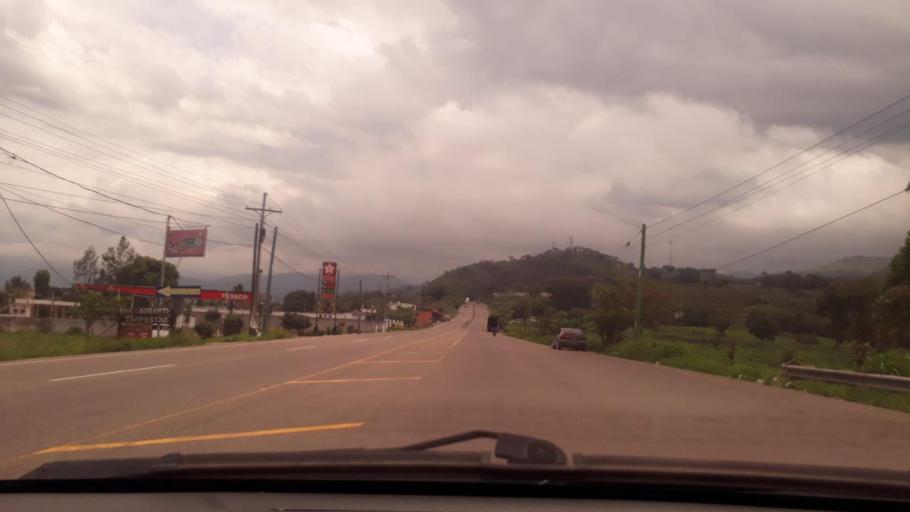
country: GT
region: Santa Rosa
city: Cuilapa
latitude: 14.2549
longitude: -90.2803
